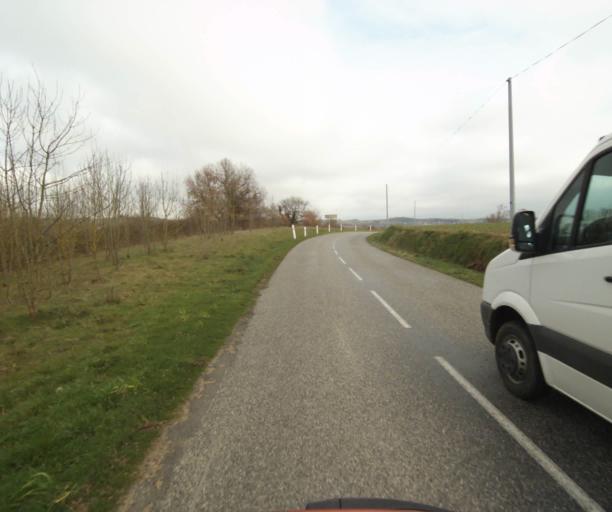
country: FR
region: Languedoc-Roussillon
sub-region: Departement de l'Aude
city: Belpech
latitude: 43.2137
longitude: 1.7233
